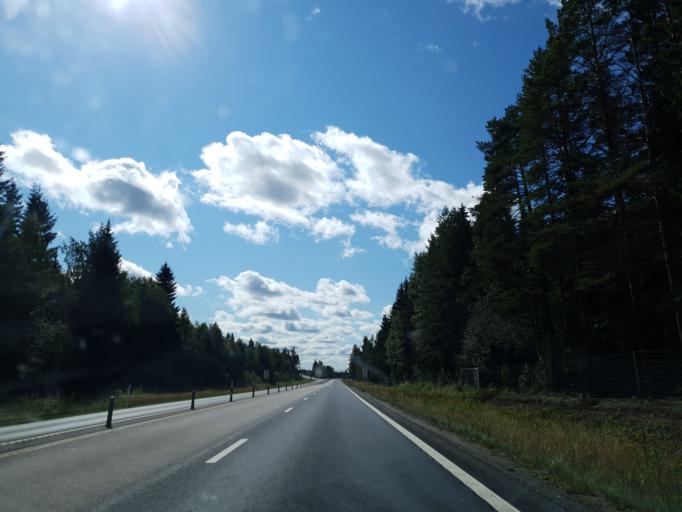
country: SE
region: Vaesterbotten
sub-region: Nordmalings Kommun
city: Nordmaling
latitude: 63.5426
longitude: 19.4075
